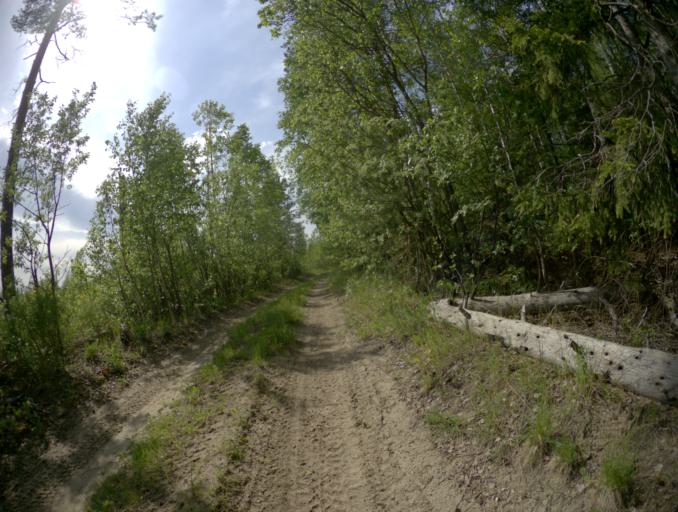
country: RU
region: Vladimir
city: Ivanishchi
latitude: 55.6874
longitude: 40.3728
